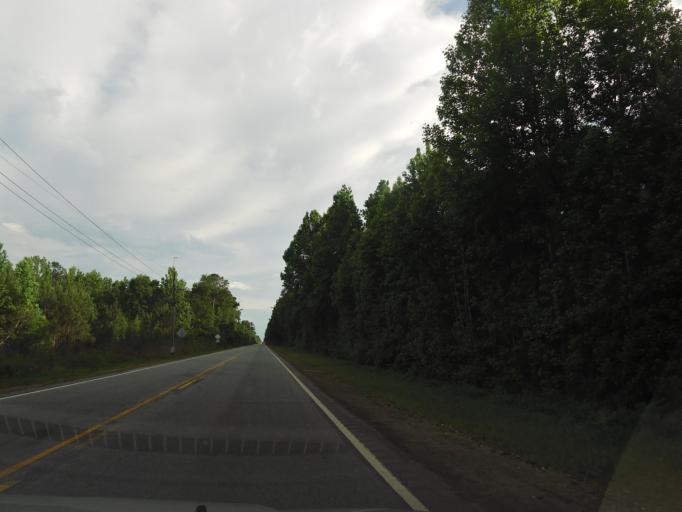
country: US
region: South Carolina
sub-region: Hampton County
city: Estill
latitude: 32.7249
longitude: -81.2421
